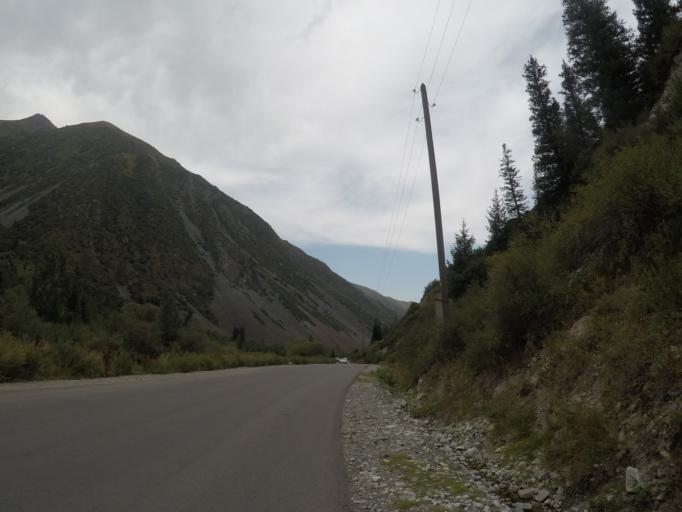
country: KG
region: Chuy
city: Bishkek
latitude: 42.5753
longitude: 74.4825
